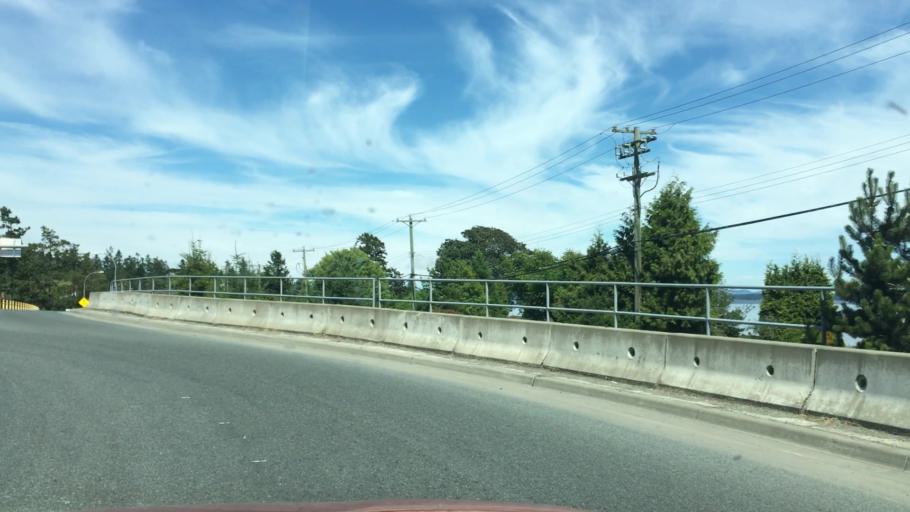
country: CA
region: British Columbia
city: North Saanich
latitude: 48.6298
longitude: -123.4110
